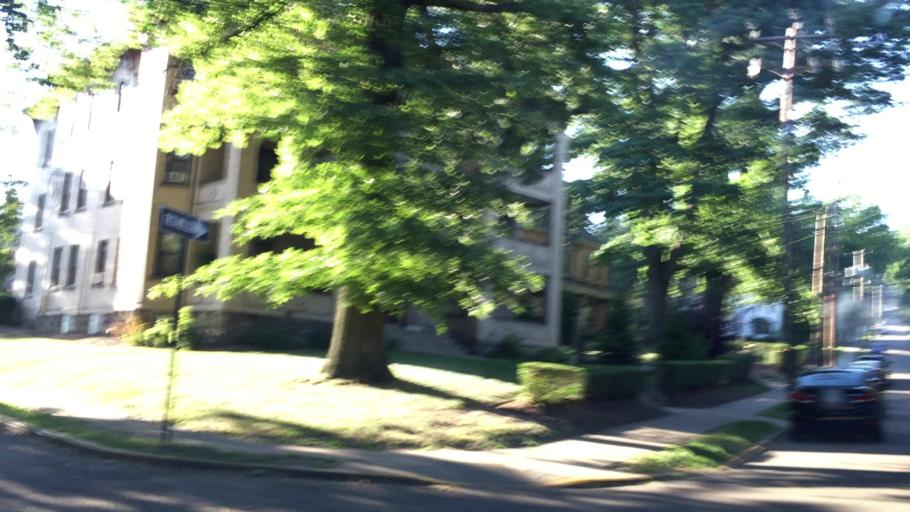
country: US
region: Pennsylvania
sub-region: Allegheny County
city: Ben Avon
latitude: 40.5068
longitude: -80.0813
